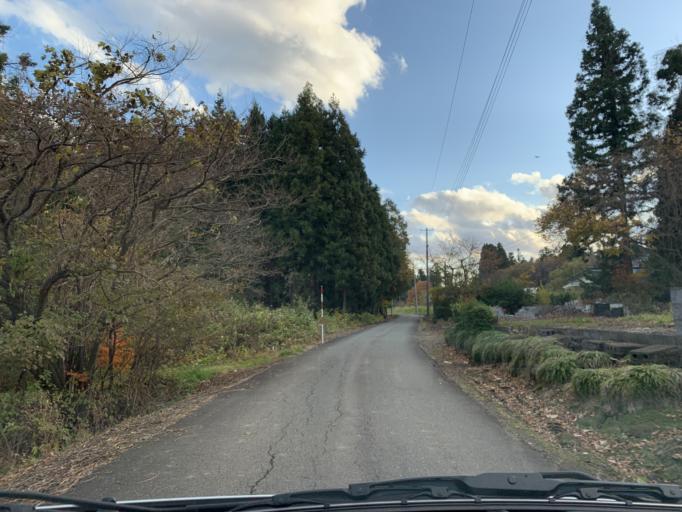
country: JP
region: Iwate
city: Mizusawa
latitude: 39.1087
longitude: 141.0394
